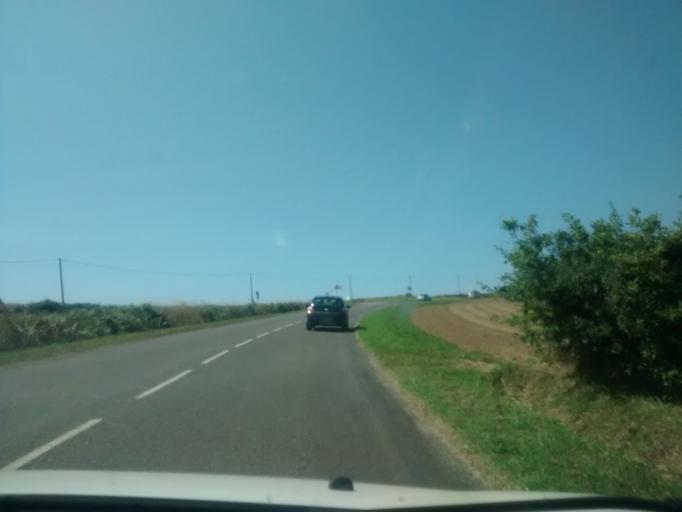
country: FR
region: Brittany
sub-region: Departement d'Ille-et-Vilaine
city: Cancale
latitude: 48.6891
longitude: -1.8785
